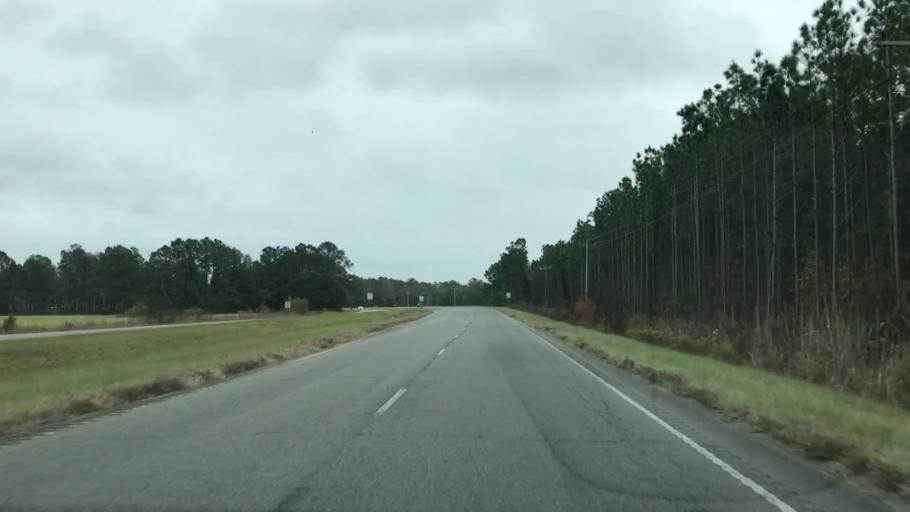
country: US
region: South Carolina
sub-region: Charleston County
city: Awendaw
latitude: 33.0387
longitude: -79.5983
